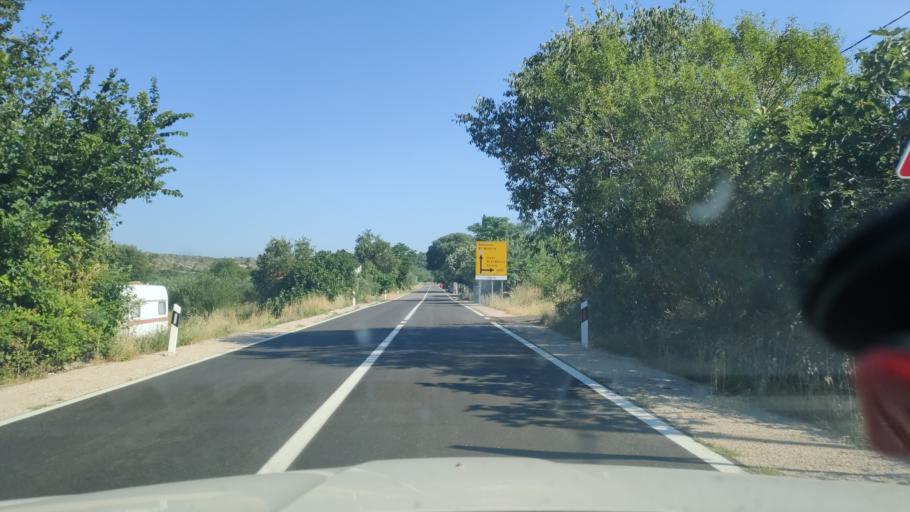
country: HR
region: Sibensko-Kniniska
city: Zaton
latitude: 43.8968
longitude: 15.8644
